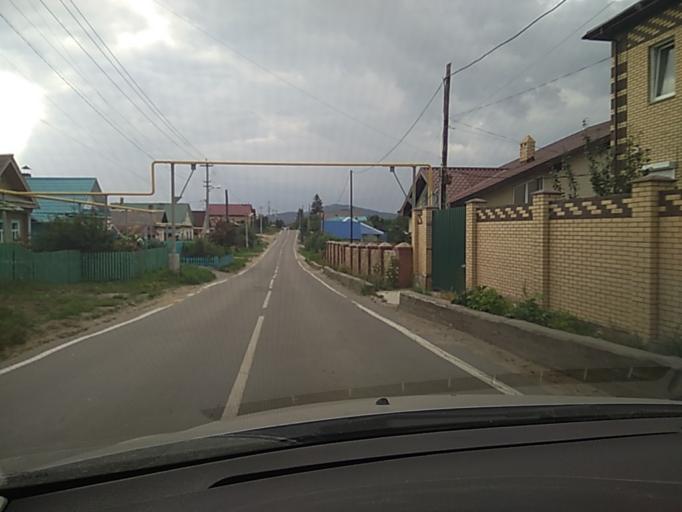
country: RU
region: Chelyabinsk
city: Kyshtym
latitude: 55.6985
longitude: 60.5383
